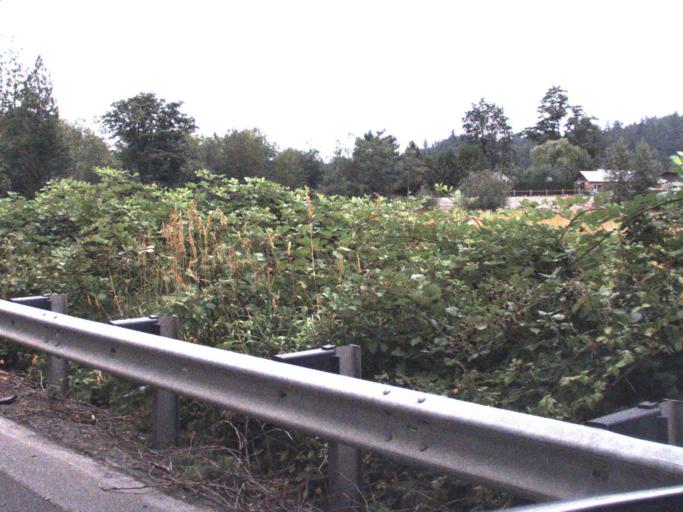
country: US
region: Washington
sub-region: King County
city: Fall City
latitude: 47.6034
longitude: -121.9134
